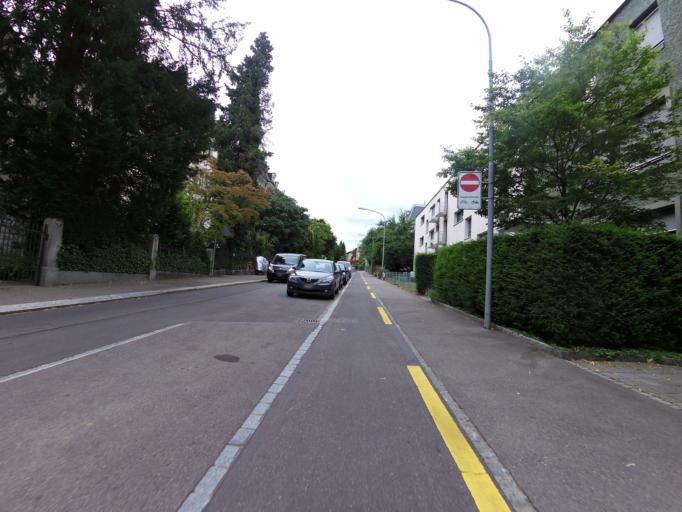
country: CH
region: Zurich
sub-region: Bezirk Zuerich
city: Zuerich (Kreis 7) / Hottingen
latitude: 47.3663
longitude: 8.5591
